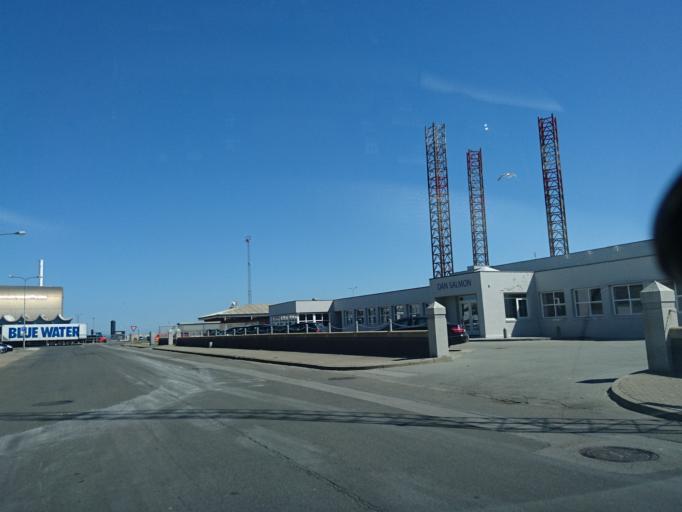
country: DK
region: North Denmark
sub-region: Hjorring Kommune
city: Hirtshals
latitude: 57.5918
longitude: 9.9769
